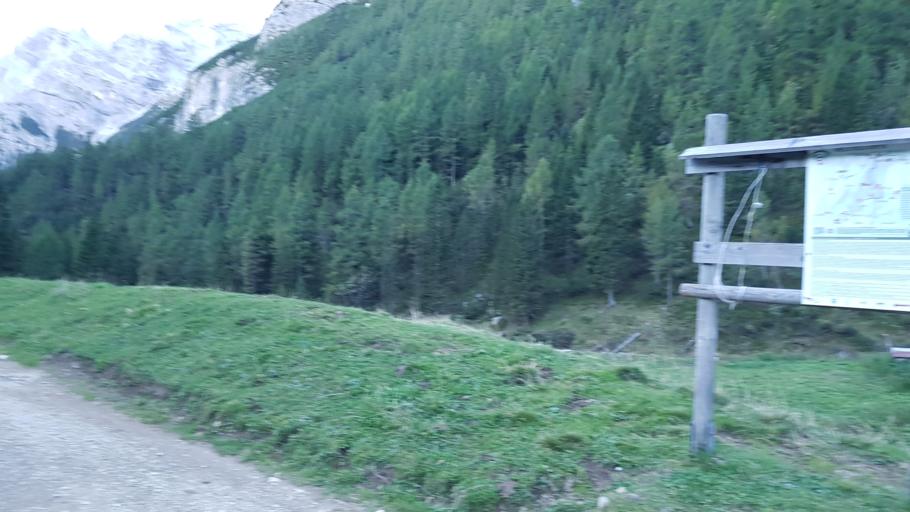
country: IT
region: Veneto
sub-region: Provincia di Belluno
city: Fusine
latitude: 46.3630
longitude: 12.0905
